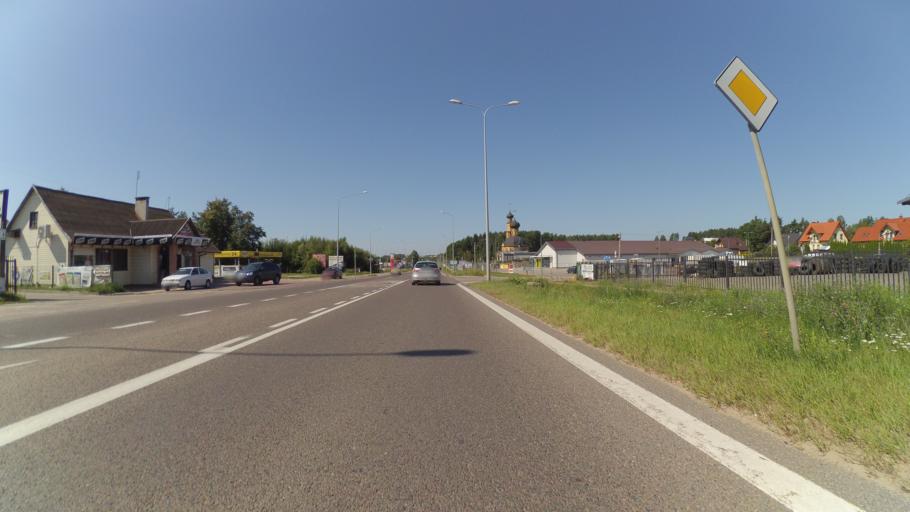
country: PL
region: Podlasie
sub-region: Bialystok
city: Bialystok
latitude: 53.1256
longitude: 23.2435
